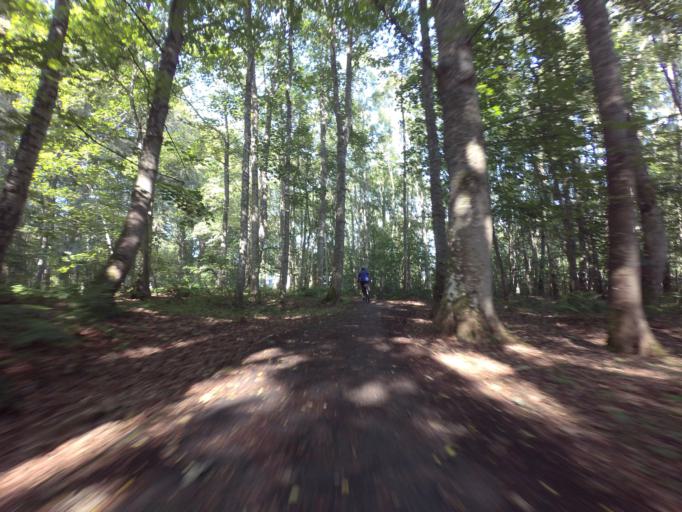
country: GB
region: Scotland
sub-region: Highland
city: Evanton
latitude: 57.6746
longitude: -4.3164
